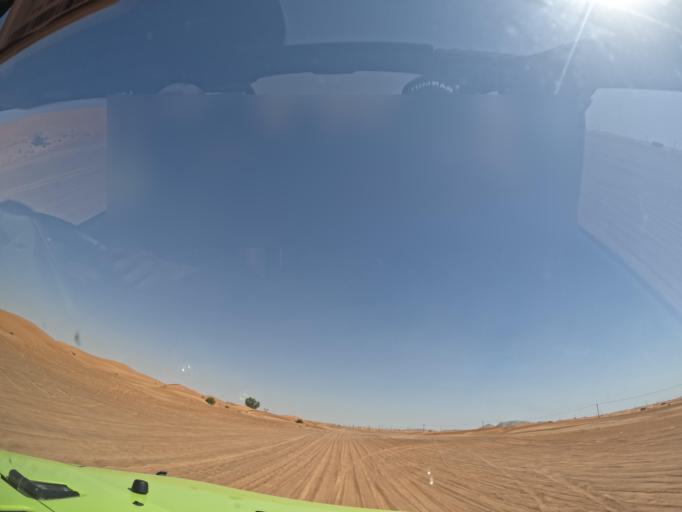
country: AE
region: Ash Shariqah
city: Adh Dhayd
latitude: 25.0048
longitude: 55.7352
